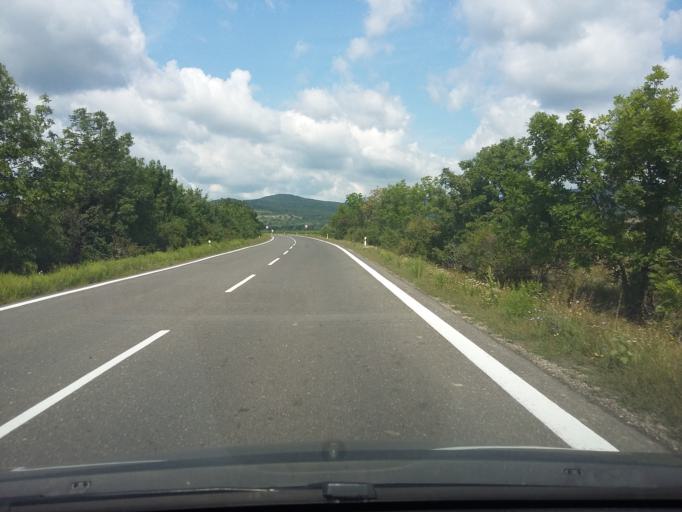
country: SK
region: Bratislavsky
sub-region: Okres Pezinok
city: Pezinok
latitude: 48.3060
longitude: 17.2767
